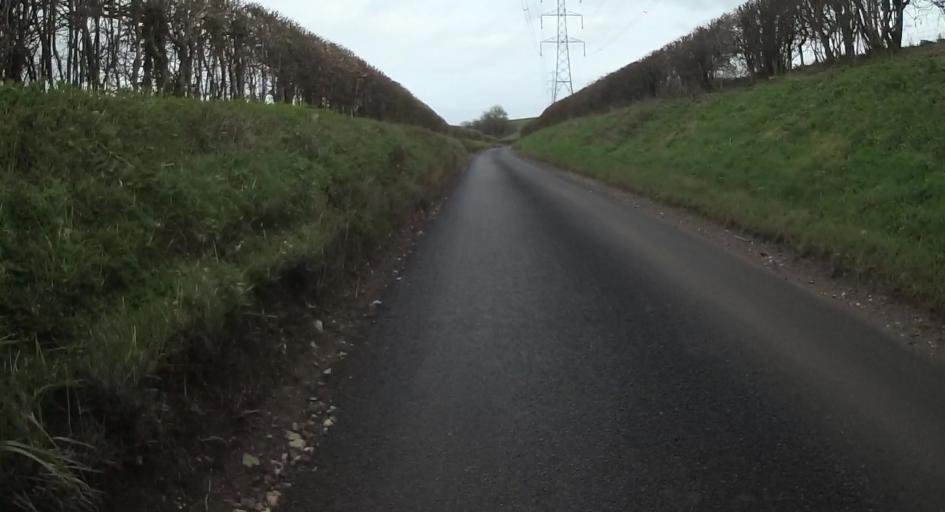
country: GB
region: England
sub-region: Hampshire
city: Kingsclere
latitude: 51.3034
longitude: -1.2213
